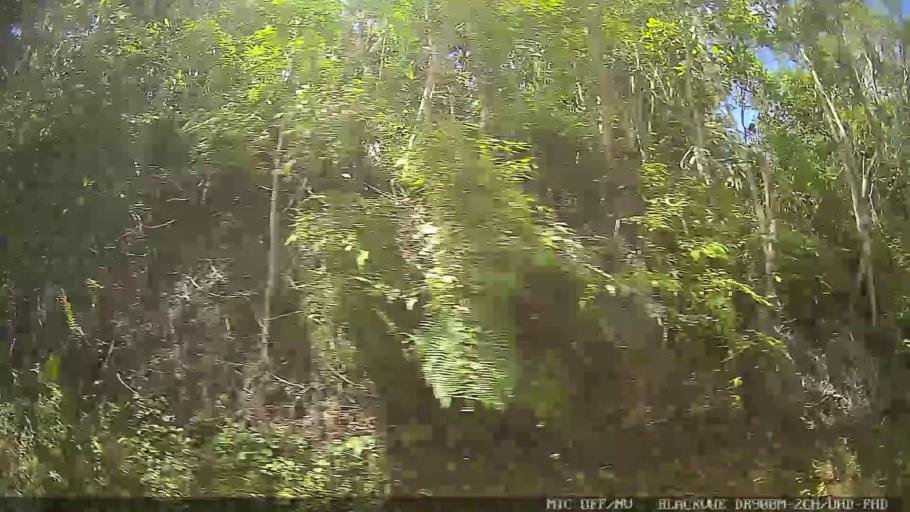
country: BR
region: Sao Paulo
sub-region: Caraguatatuba
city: Caraguatatuba
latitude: -23.5377
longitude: -45.5789
